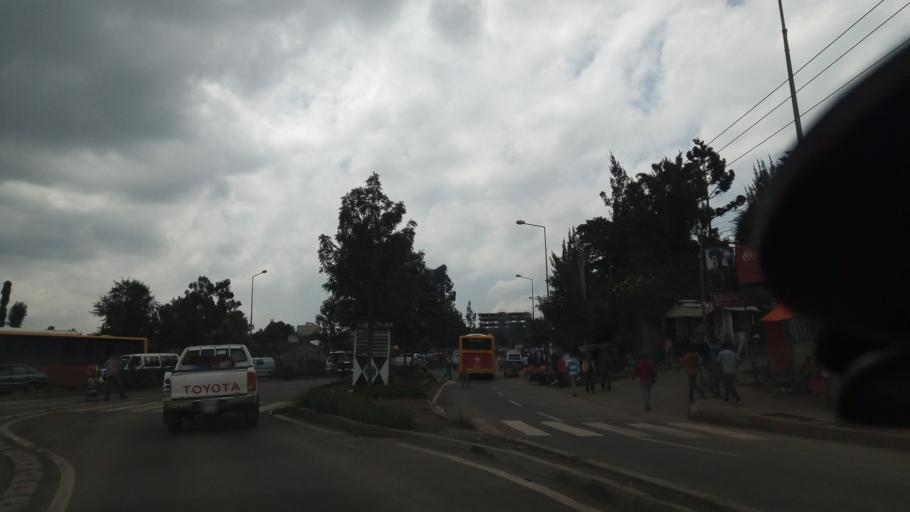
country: ET
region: Adis Abeba
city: Addis Ababa
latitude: 8.9925
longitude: 38.7170
